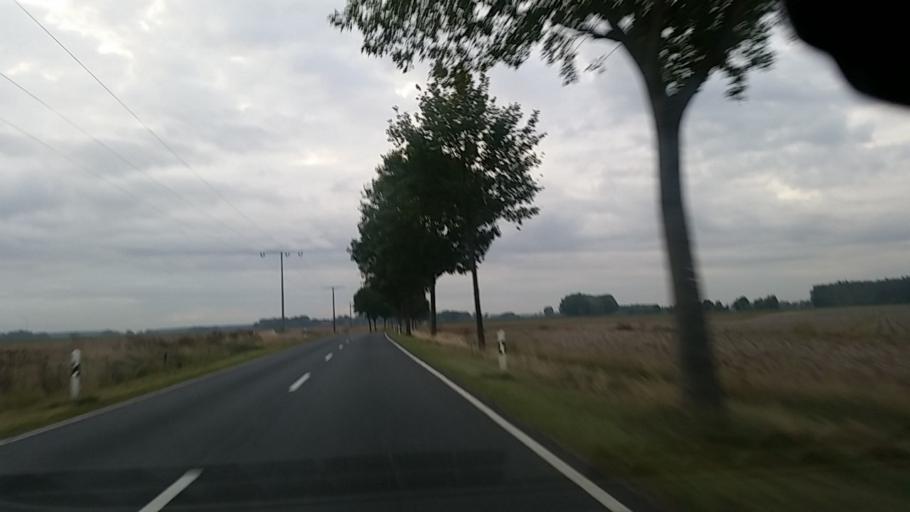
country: DE
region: Lower Saxony
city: Sprakensehl
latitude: 52.7618
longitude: 10.5013
